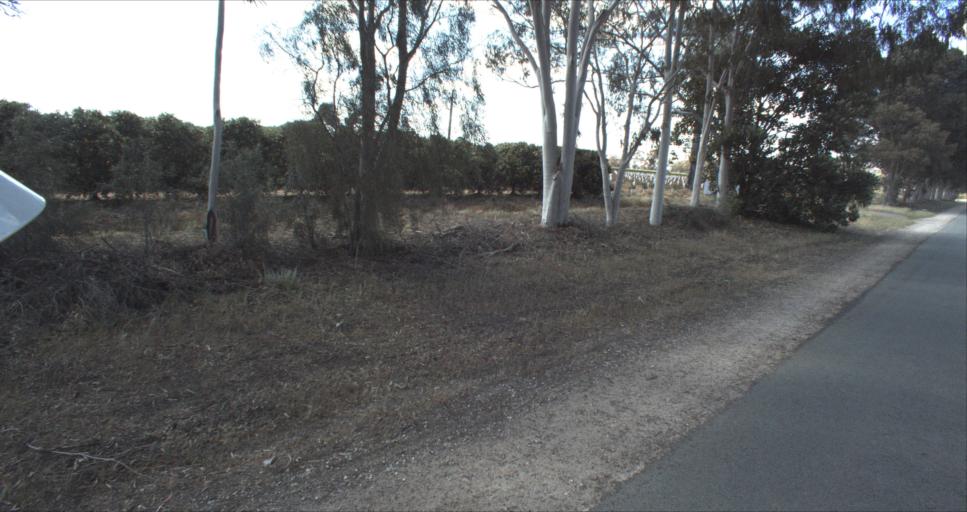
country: AU
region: New South Wales
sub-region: Leeton
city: Leeton
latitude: -34.5101
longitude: 146.2287
